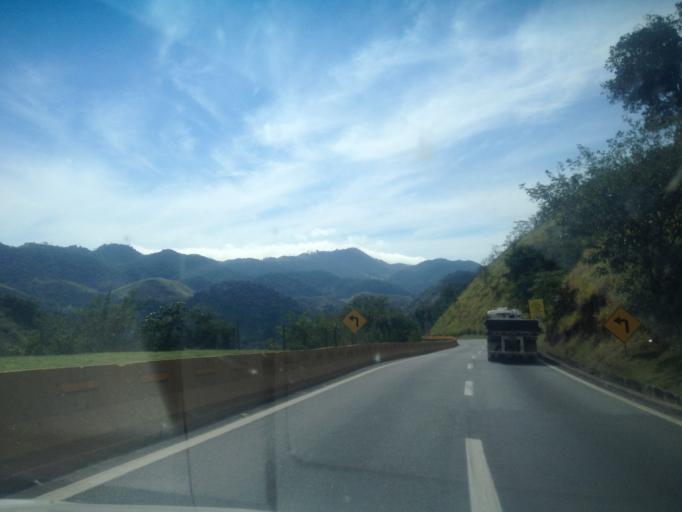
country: BR
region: Rio de Janeiro
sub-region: Pirai
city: Pirai
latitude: -22.6701
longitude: -43.8301
